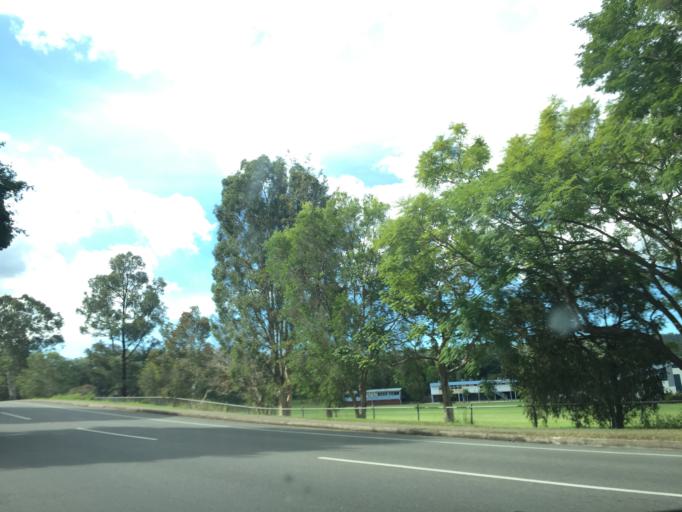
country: AU
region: Queensland
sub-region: Moreton Bay
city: Ferny Hills
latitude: -27.4376
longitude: 152.9349
